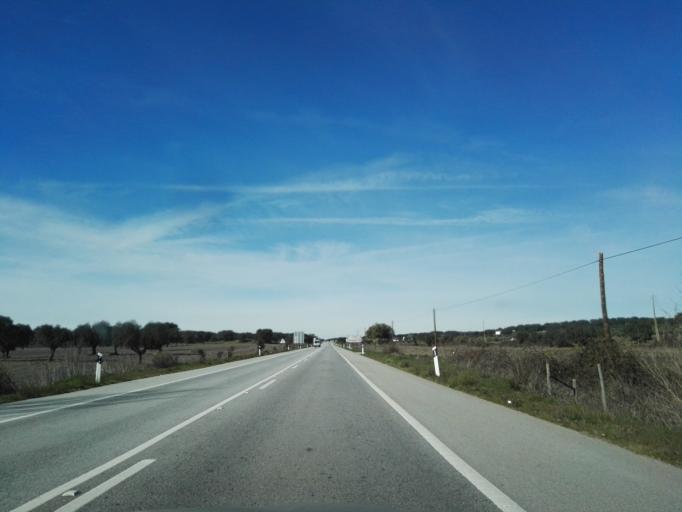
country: PT
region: Portalegre
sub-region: Arronches
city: Arronches
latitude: 39.1609
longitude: -7.3217
